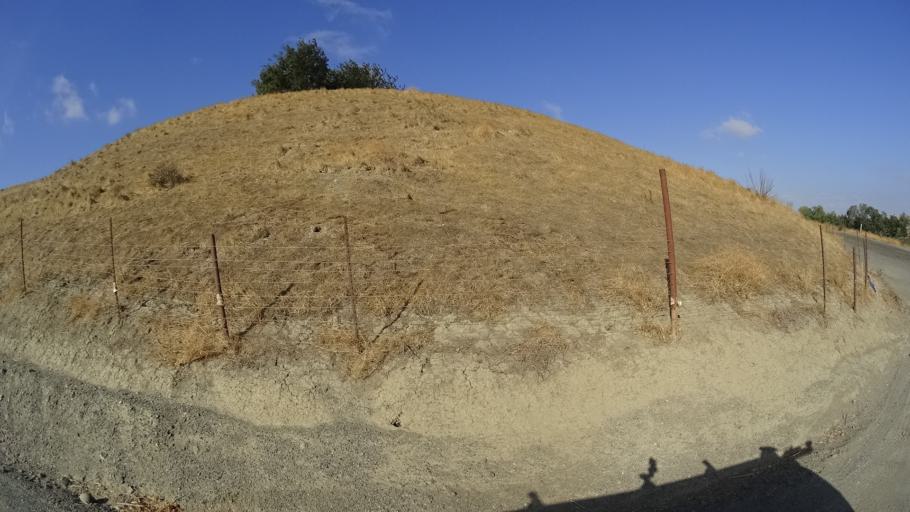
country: US
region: California
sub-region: Yolo County
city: Dunnigan
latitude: 38.8034
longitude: -122.0066
